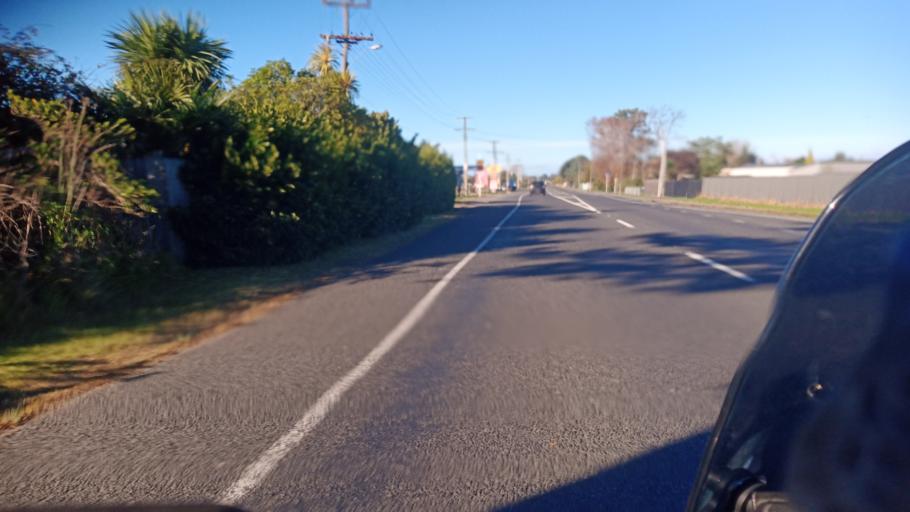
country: NZ
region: Hawke's Bay
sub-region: Napier City
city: Napier
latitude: -39.4222
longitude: 176.8681
